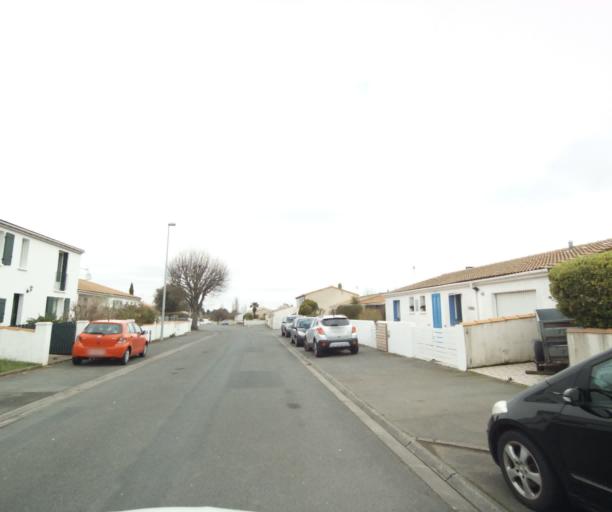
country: FR
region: Poitou-Charentes
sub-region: Departement de la Charente-Maritime
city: Lagord
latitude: 46.1890
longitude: -1.1492
